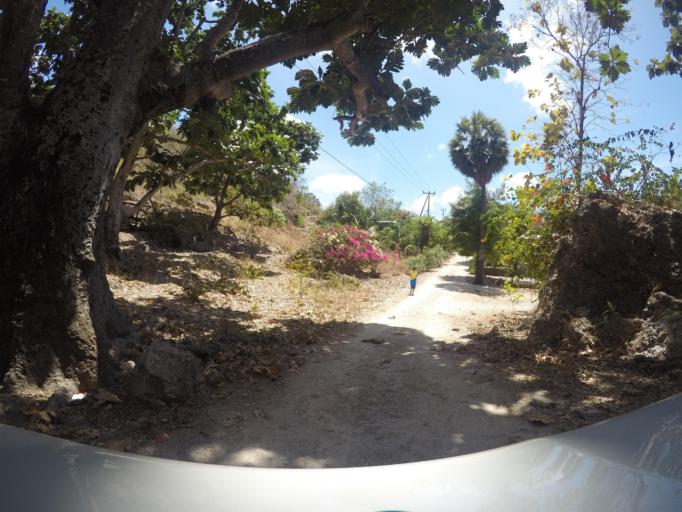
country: TL
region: Baucau
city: Baucau
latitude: -8.4496
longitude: 126.4395
